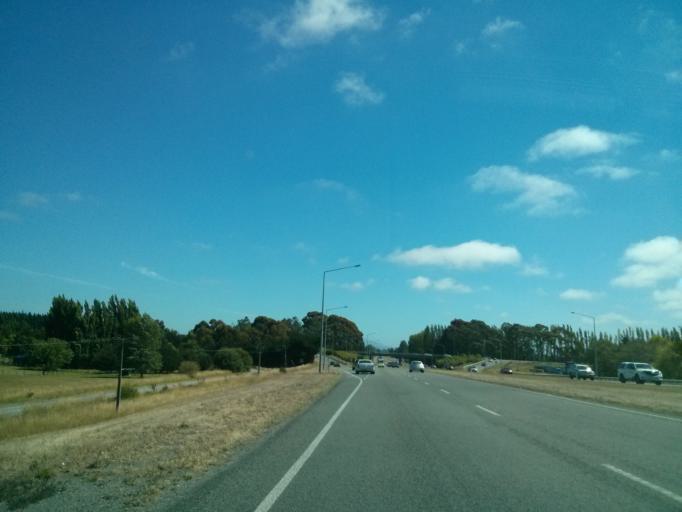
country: NZ
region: Canterbury
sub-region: Waimakariri District
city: Kaiapoi
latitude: -43.4115
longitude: 172.6455
